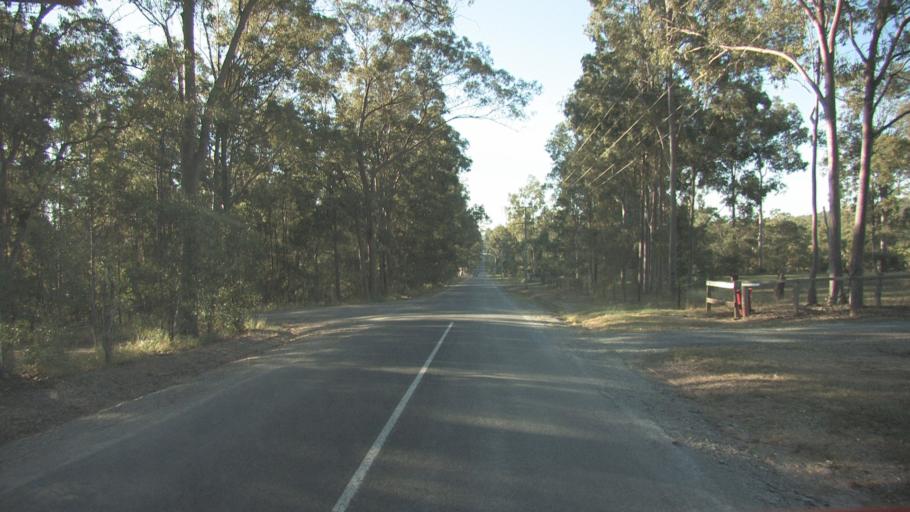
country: AU
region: Queensland
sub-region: Logan
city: Chambers Flat
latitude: -27.7769
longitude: 153.1362
